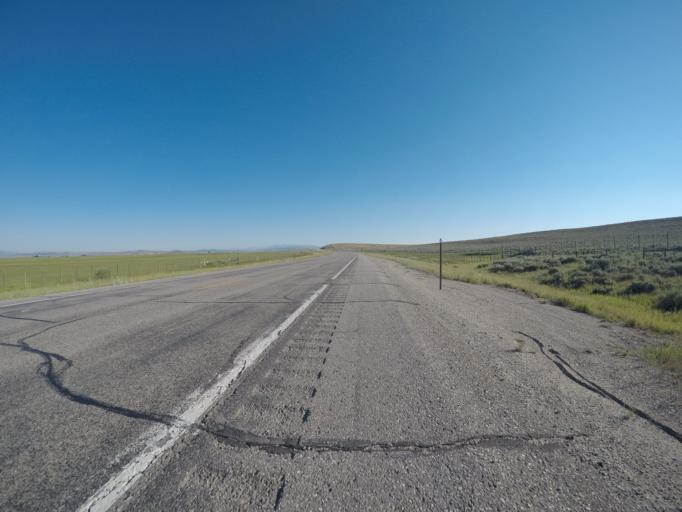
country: US
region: Wyoming
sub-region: Sublette County
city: Pinedale
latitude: 42.9344
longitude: -110.0813
